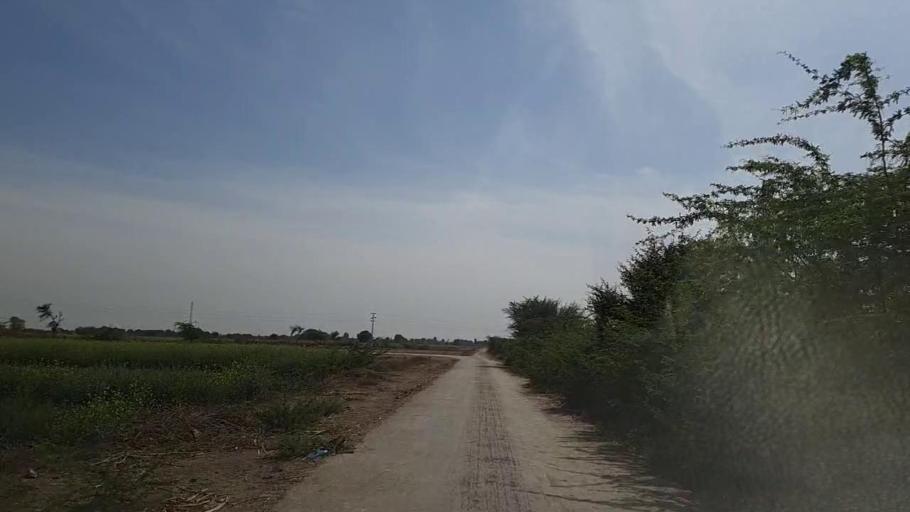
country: PK
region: Sindh
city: Samaro
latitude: 25.2036
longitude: 69.4501
